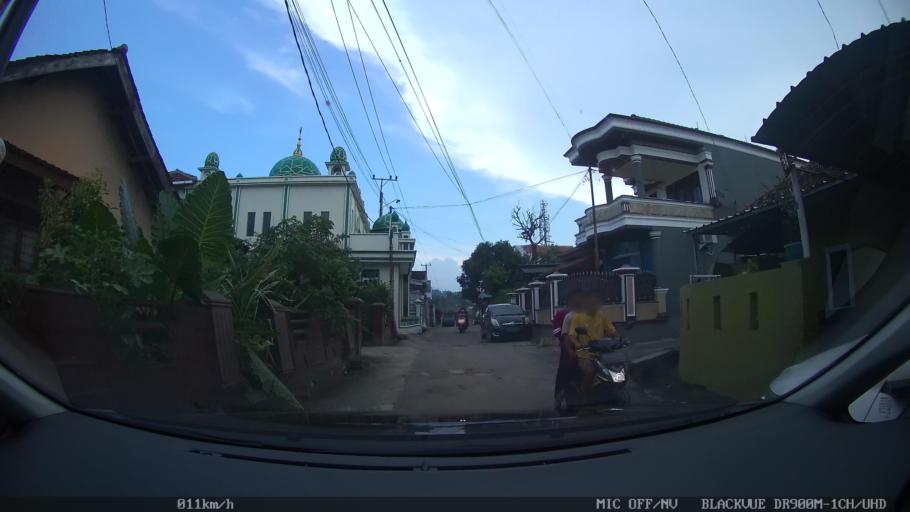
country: ID
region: Lampung
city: Kedaton
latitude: -5.3944
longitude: 105.2193
